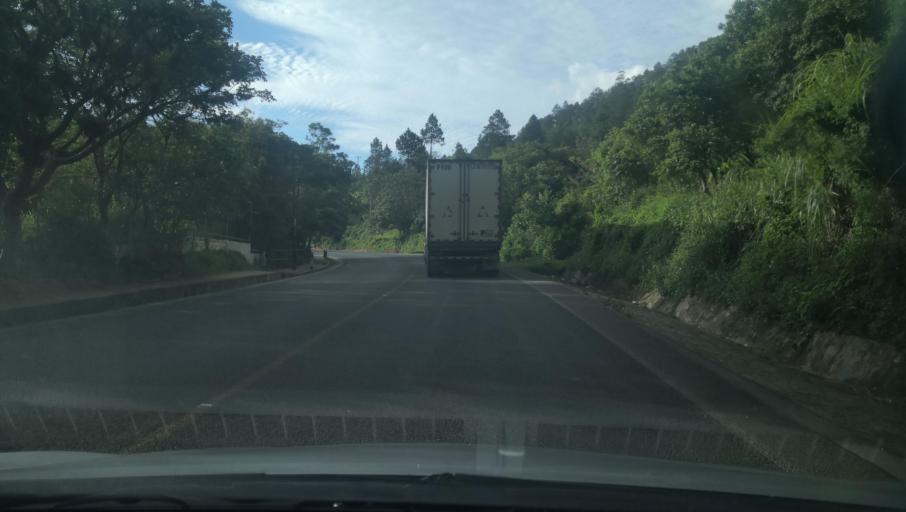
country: NI
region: Nueva Segovia
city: Mozonte
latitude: 13.7294
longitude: -86.5102
